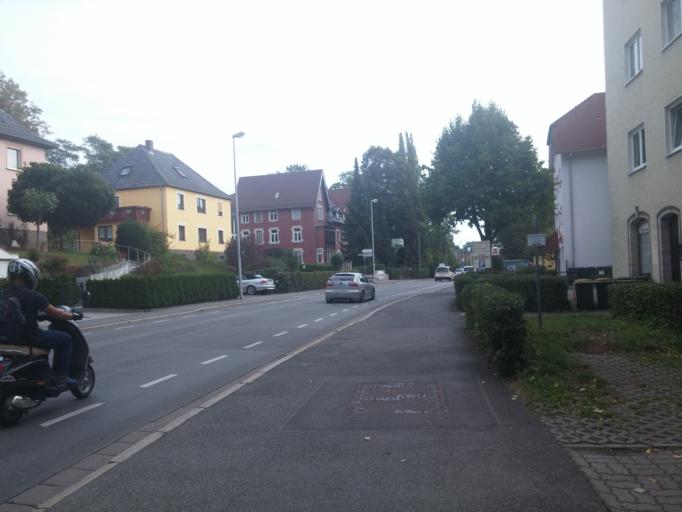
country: DE
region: Bavaria
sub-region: Upper Franconia
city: Coburg
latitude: 50.2491
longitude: 10.9696
